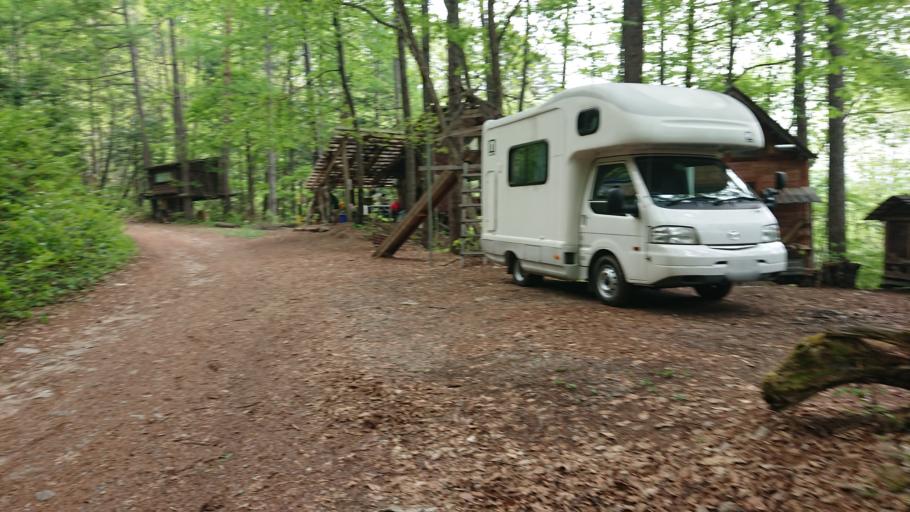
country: JP
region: Nagano
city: Omachi
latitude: 36.5074
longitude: 137.7981
